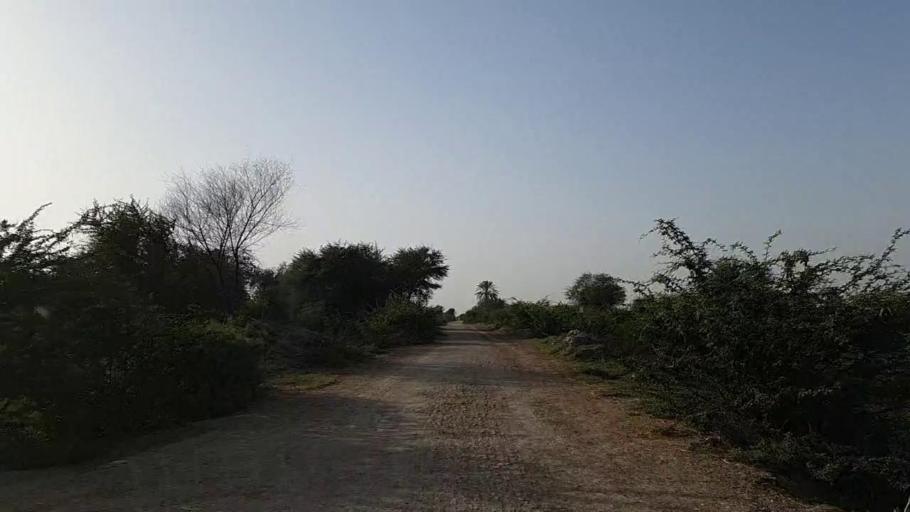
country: PK
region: Sindh
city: Jati
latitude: 24.3449
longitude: 68.1438
